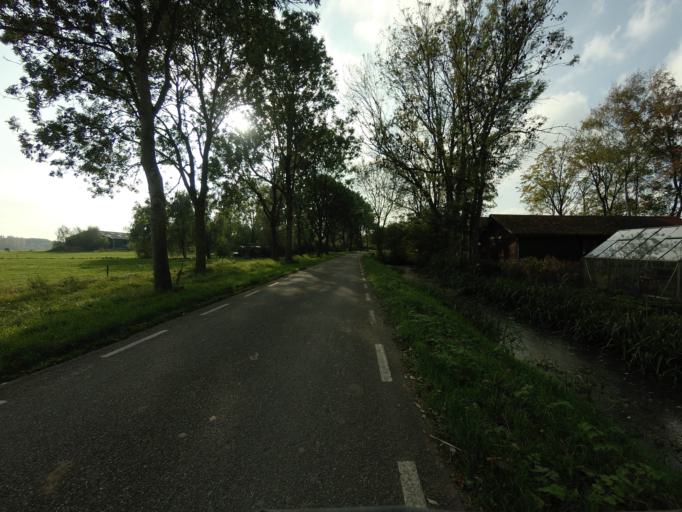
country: NL
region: Gelderland
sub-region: Gemeente Culemborg
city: Culemborg
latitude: 51.9272
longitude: 5.2146
